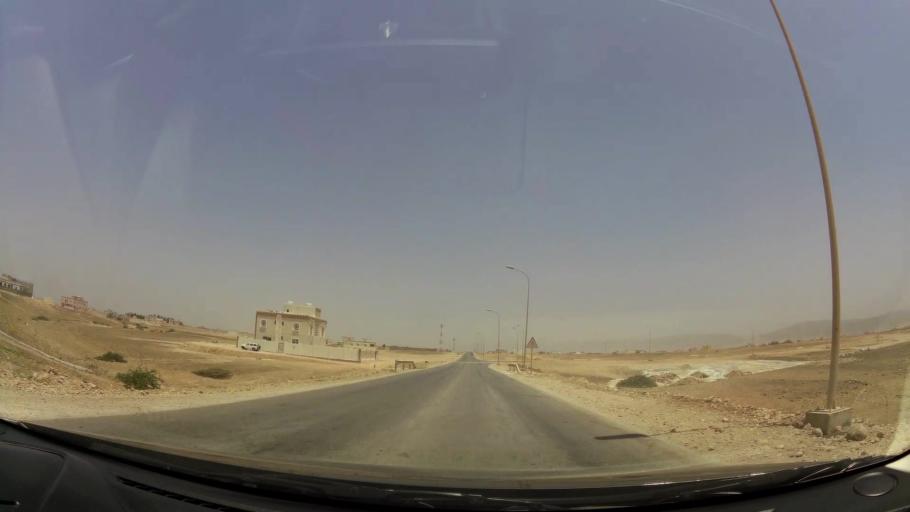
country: OM
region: Zufar
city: Salalah
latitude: 17.0916
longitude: 54.1934
